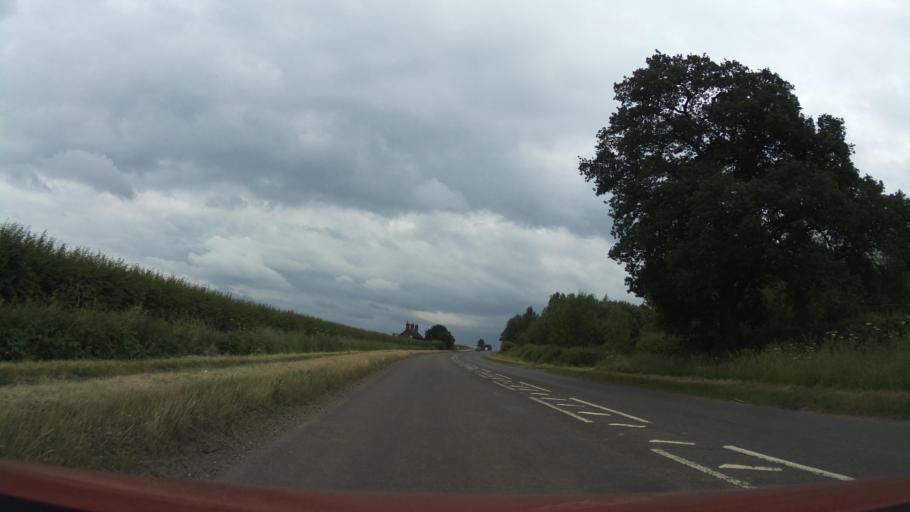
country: GB
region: England
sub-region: Staffordshire
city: Penkridge
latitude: 52.7448
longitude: -2.1078
